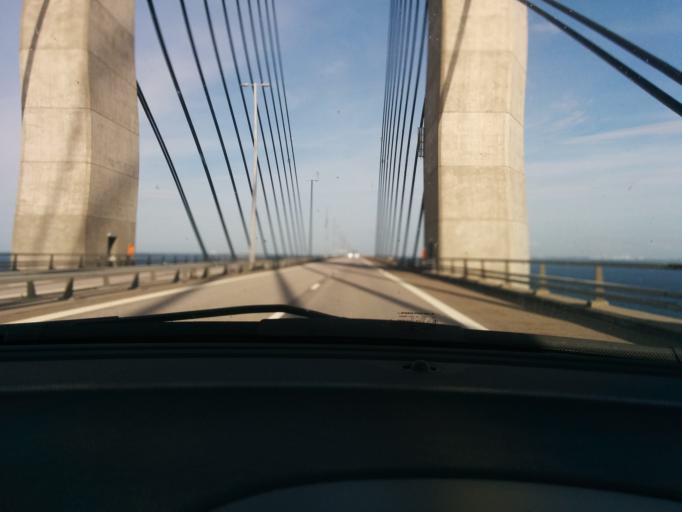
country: SE
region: Skane
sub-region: Malmo
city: Bunkeflostrand
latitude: 55.5759
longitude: 12.8241
